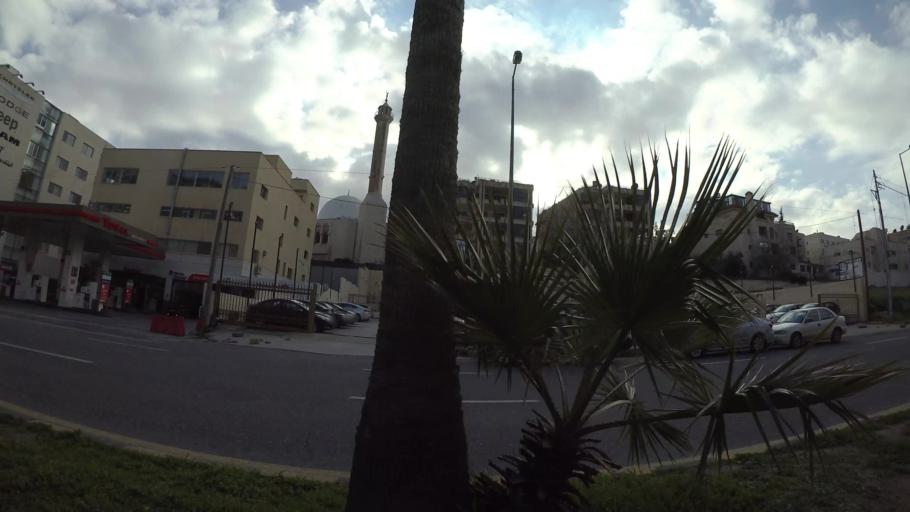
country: JO
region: Amman
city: Amman
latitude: 31.9631
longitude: 35.8894
